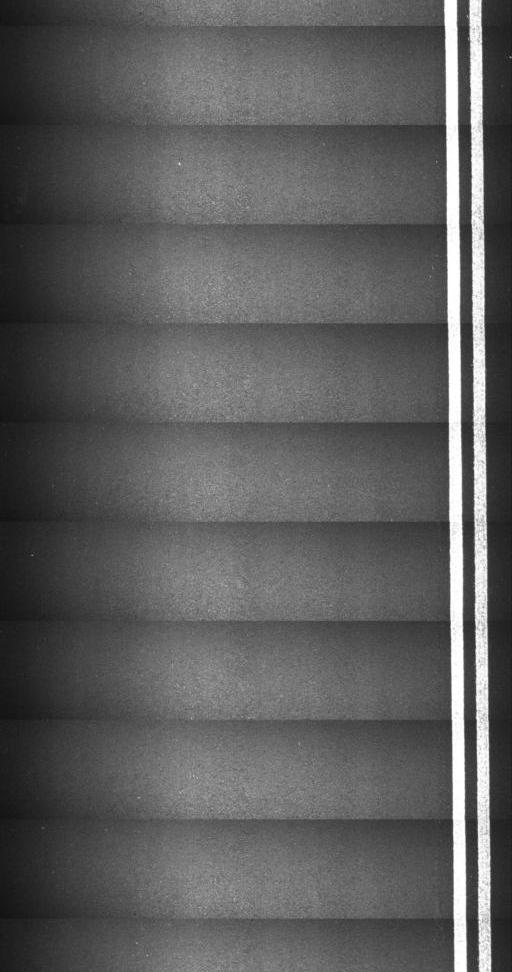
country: US
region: Vermont
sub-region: Orange County
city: Randolph
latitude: 43.8345
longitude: -72.6436
